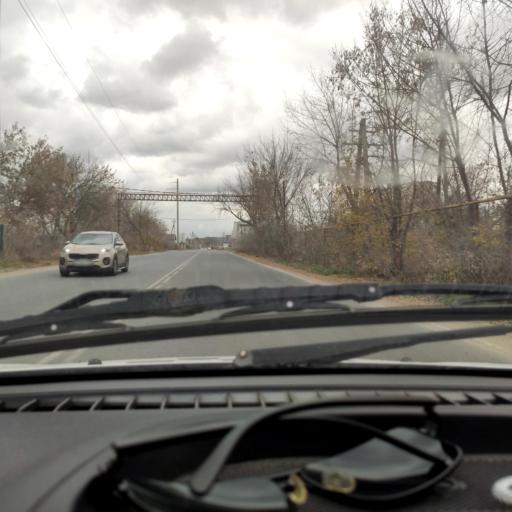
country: RU
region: Samara
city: Zhigulevsk
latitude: 53.5270
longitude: 49.4787
